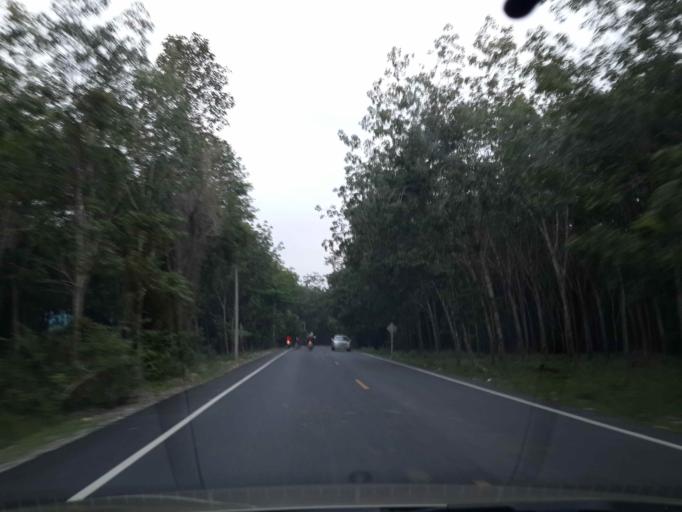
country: TH
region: Narathiwat
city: Rueso
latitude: 6.3514
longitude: 101.4740
